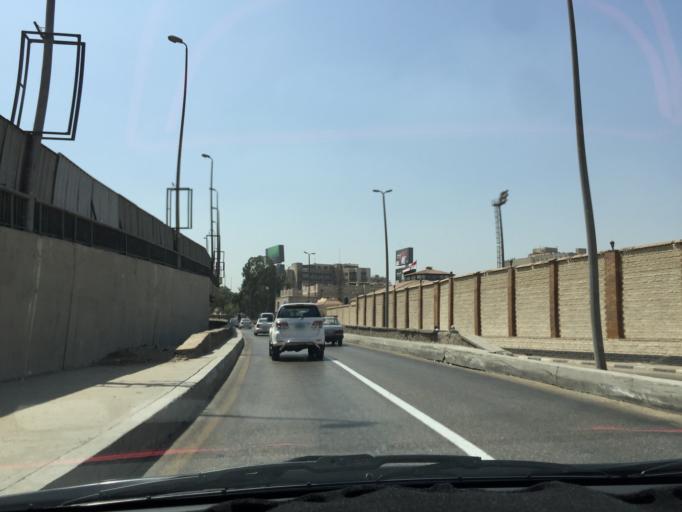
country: EG
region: Muhafazat al Qahirah
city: Cairo
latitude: 30.0713
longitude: 31.2942
